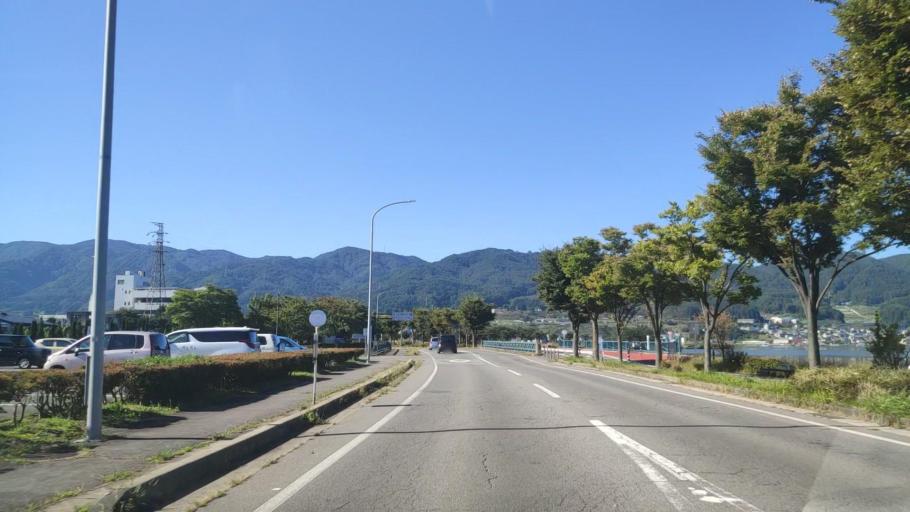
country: JP
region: Nagano
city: Suwa
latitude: 36.0364
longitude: 138.0904
